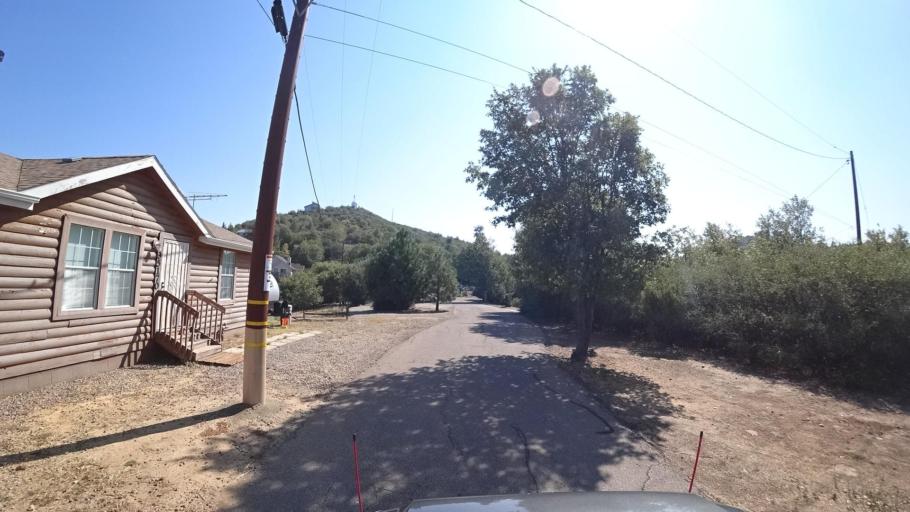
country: US
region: California
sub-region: San Diego County
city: Julian
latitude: 33.0269
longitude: -116.5703
